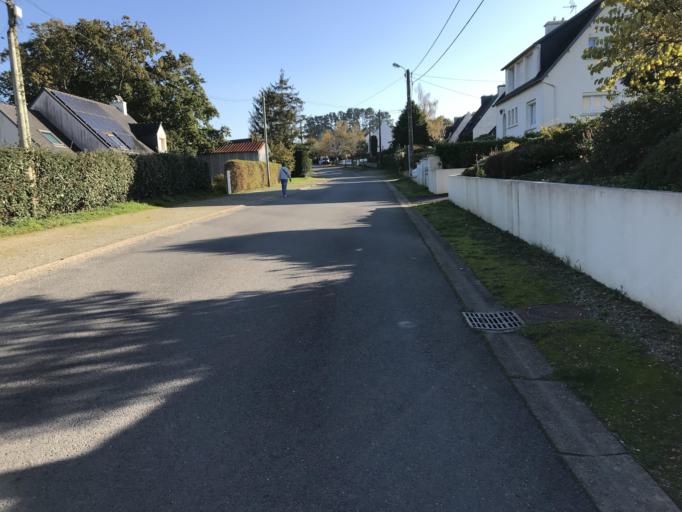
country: FR
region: Brittany
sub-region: Departement du Finistere
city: Hopital-Camfrout
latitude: 48.3261
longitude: -4.2382
